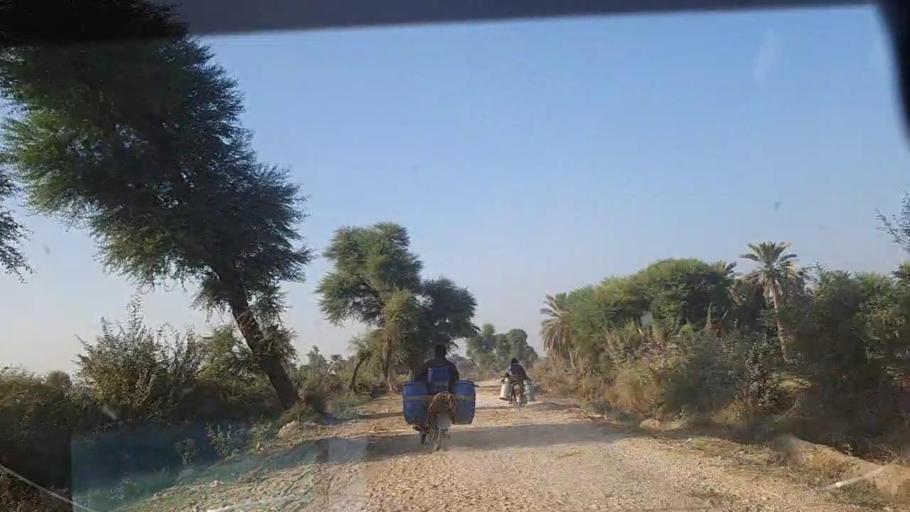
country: PK
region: Sindh
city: Sobhadero
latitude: 27.2664
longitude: 68.3486
